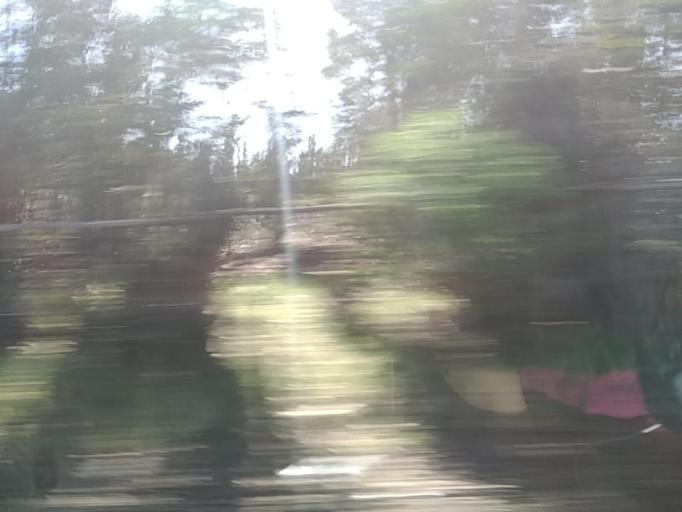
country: CL
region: Valparaiso
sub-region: San Antonio Province
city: El Tabo
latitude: -33.4127
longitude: -71.6114
